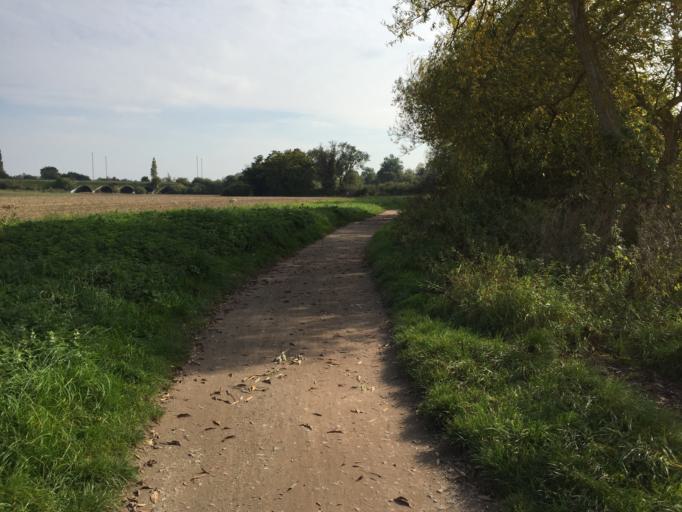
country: GB
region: England
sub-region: West Berkshire
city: Eton
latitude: 51.4915
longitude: -0.6268
